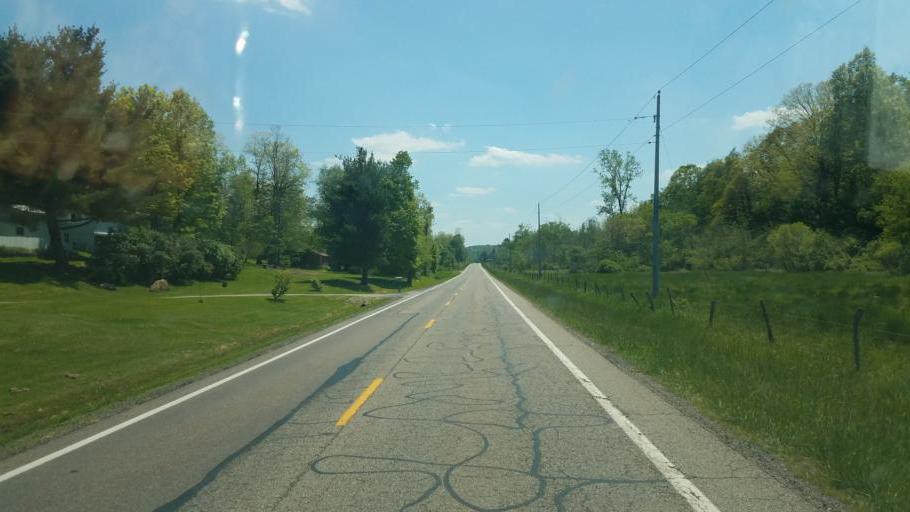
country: US
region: Ohio
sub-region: Muskingum County
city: Frazeysburg
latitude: 40.1886
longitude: -82.2304
